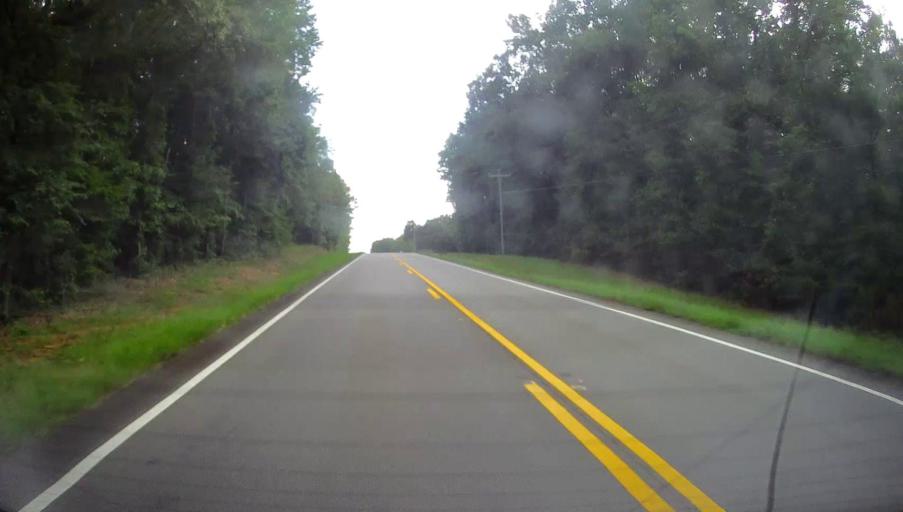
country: US
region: Georgia
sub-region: Monroe County
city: Forsyth
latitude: 32.9866
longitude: -83.9512
